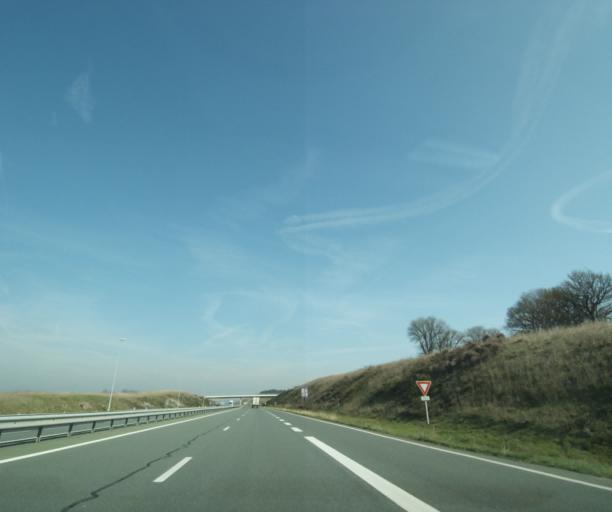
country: FR
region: Midi-Pyrenees
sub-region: Departement du Lot
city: Le Vigan
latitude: 44.6626
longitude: 1.5682
